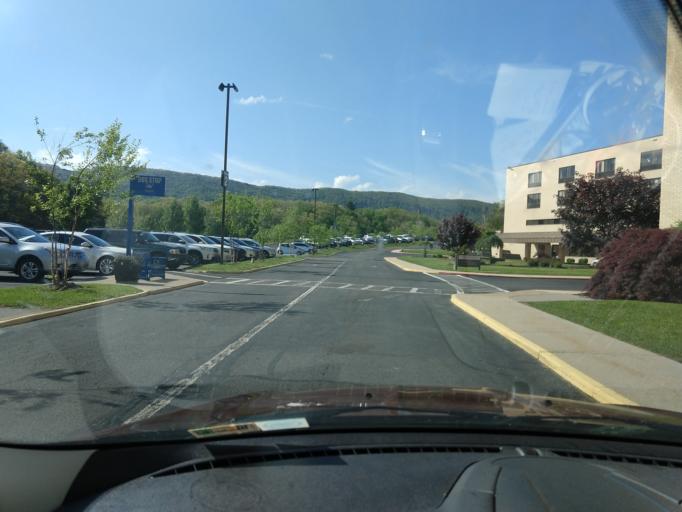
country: US
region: West Virginia
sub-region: Mercer County
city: Bluefield
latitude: 37.2564
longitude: -81.2348
